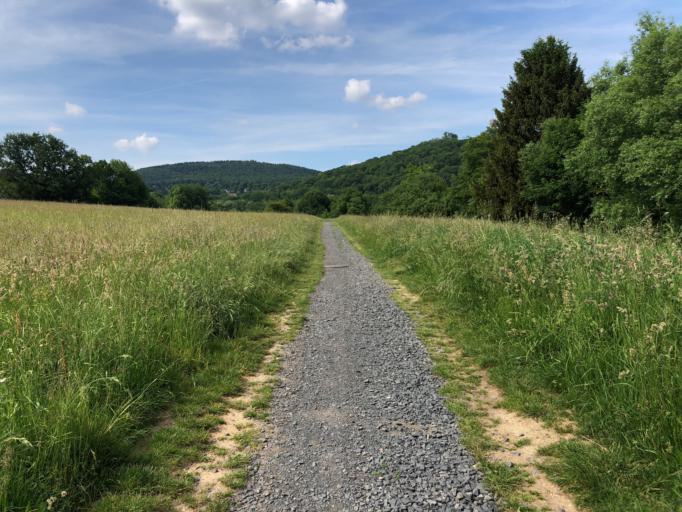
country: DE
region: Hesse
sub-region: Regierungsbezirk Darmstadt
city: Konigstein im Taunus
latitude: 50.1744
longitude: 8.4568
